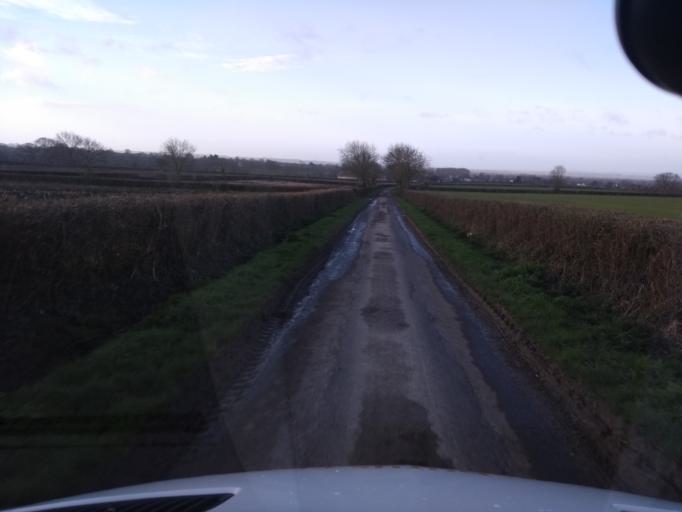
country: GB
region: England
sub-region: Somerset
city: Wedmore
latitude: 51.2339
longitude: -2.8335
